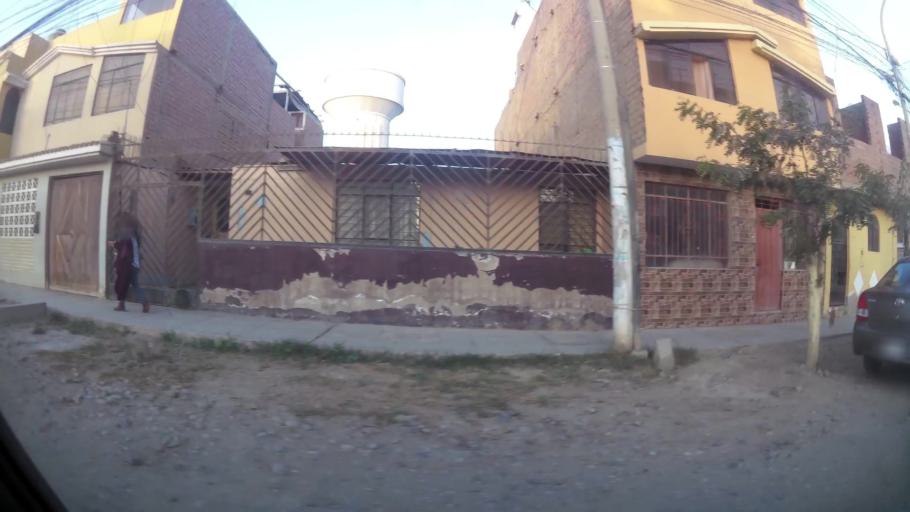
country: PE
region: Lima
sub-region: Huaura
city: Huacho
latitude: -11.1177
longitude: -77.6075
